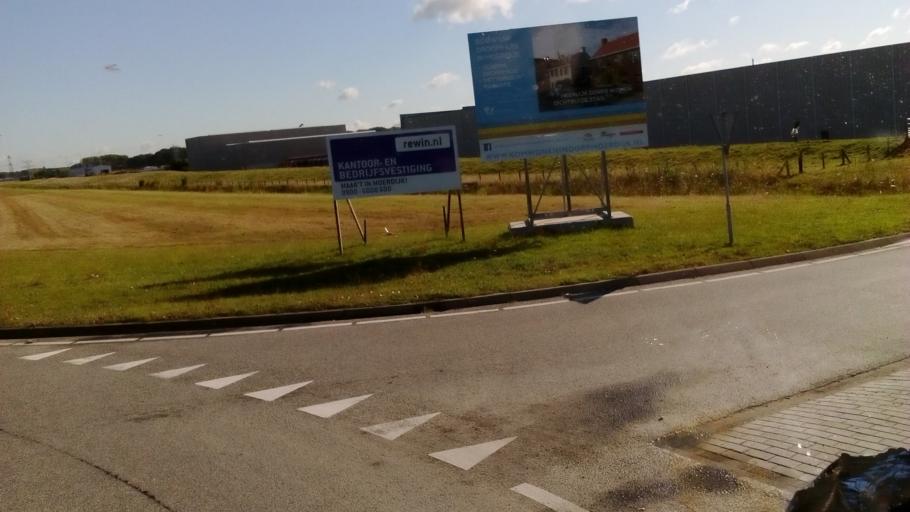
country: NL
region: North Brabant
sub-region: Gemeente Moerdijk
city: Klundert
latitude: 51.6610
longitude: 4.5635
